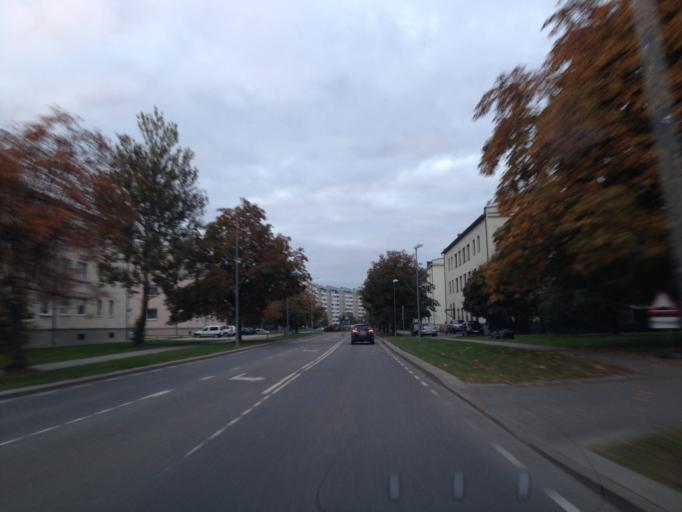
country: EE
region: Harju
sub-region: Tallinna linn
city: Tallinn
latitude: 59.4332
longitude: 24.8131
